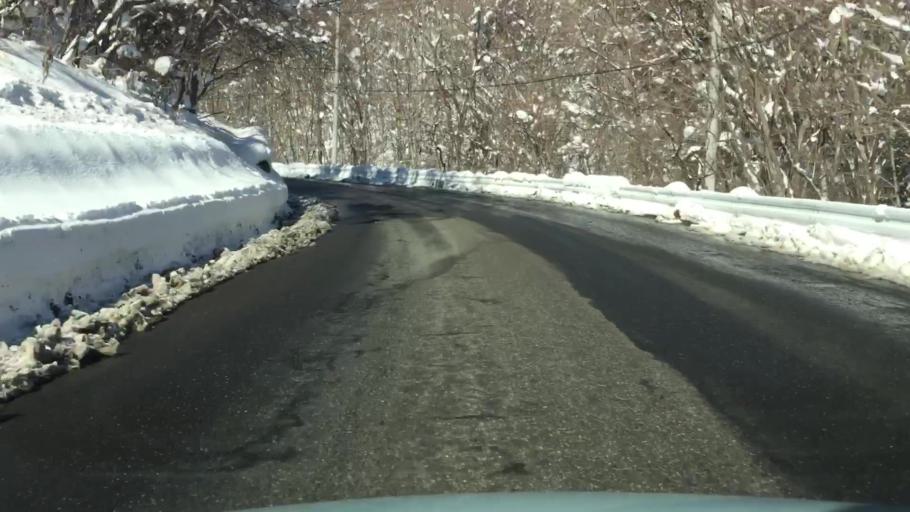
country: JP
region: Gunma
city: Numata
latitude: 36.7451
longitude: 138.9484
